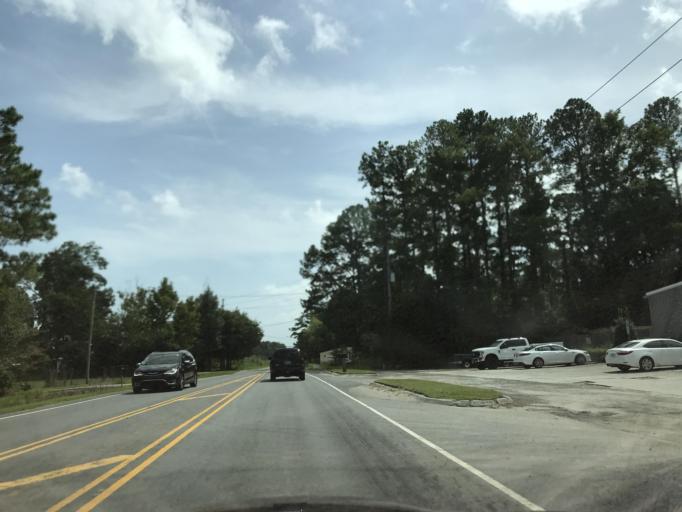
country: US
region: North Carolina
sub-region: New Hanover County
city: Wrightsboro
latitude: 34.3101
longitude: -77.9221
